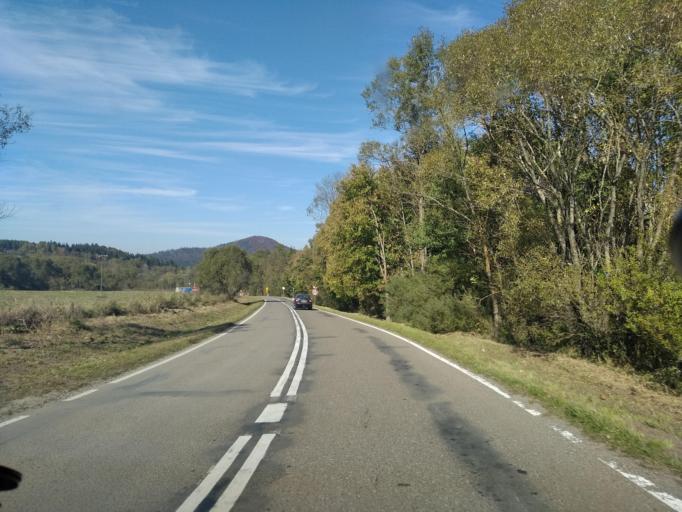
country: PL
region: Subcarpathian Voivodeship
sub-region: Powiat leski
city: Cisna
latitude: 49.2603
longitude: 22.2885
